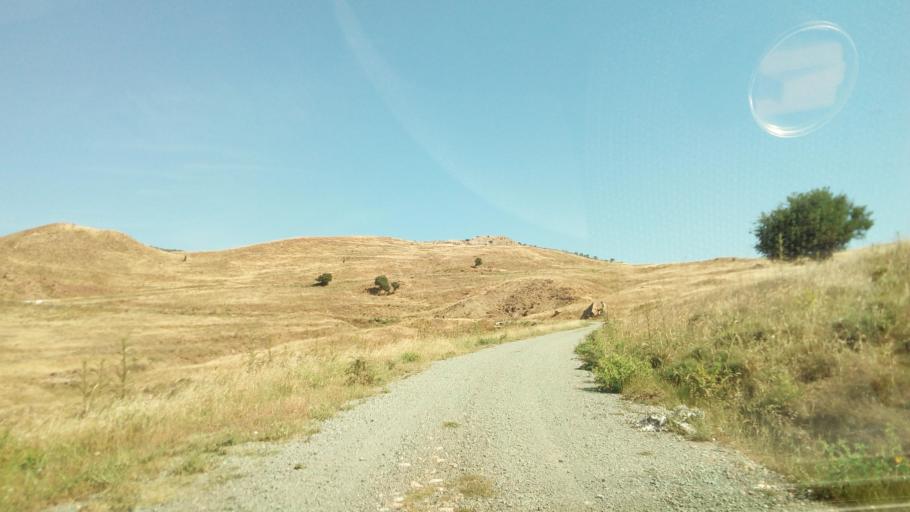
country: CY
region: Limassol
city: Pachna
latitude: 34.8140
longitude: 32.7087
